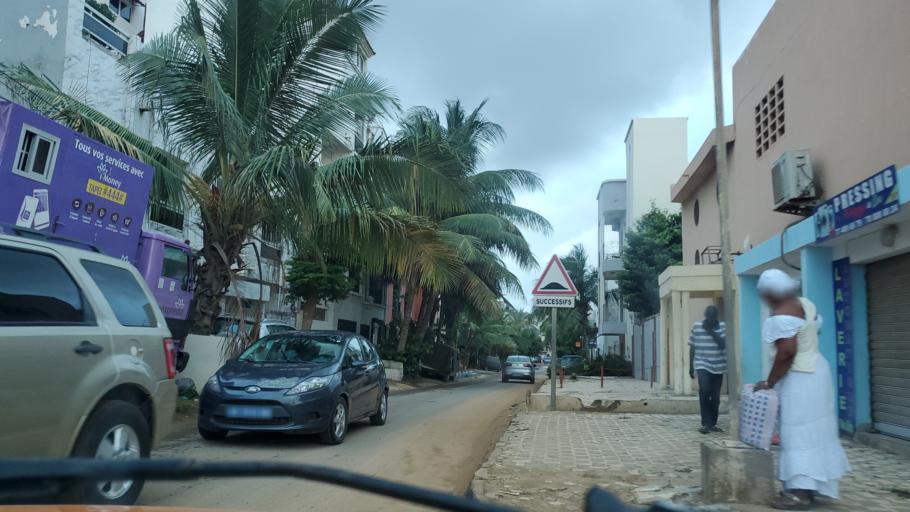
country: SN
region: Dakar
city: Mermoz Boabab
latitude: 14.7187
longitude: -17.4707
